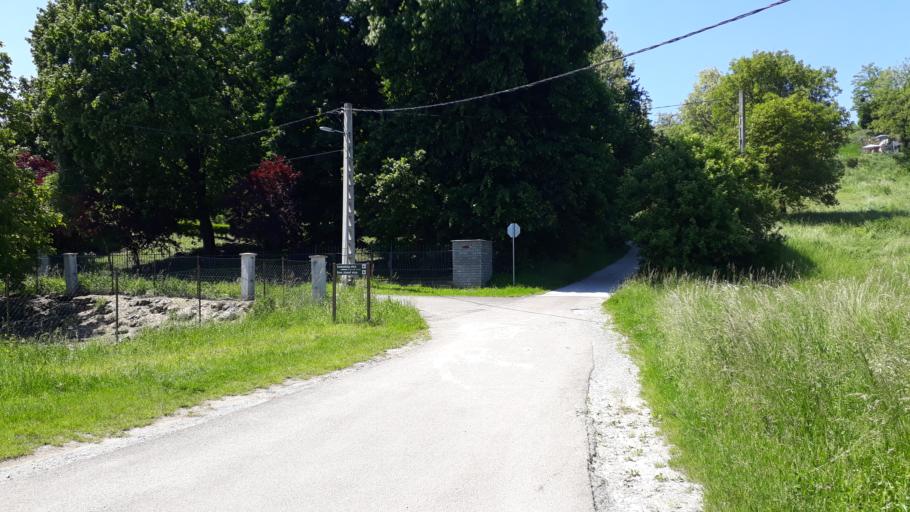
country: HU
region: Heves
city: Szilvasvarad
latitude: 48.1083
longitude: 20.3842
